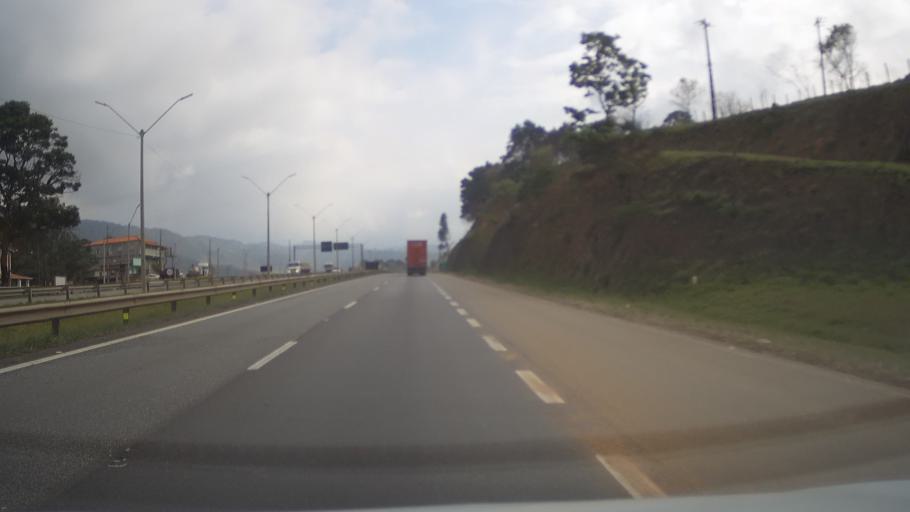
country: BR
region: Minas Gerais
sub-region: Extrema
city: Extrema
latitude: -22.9029
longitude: -46.4212
